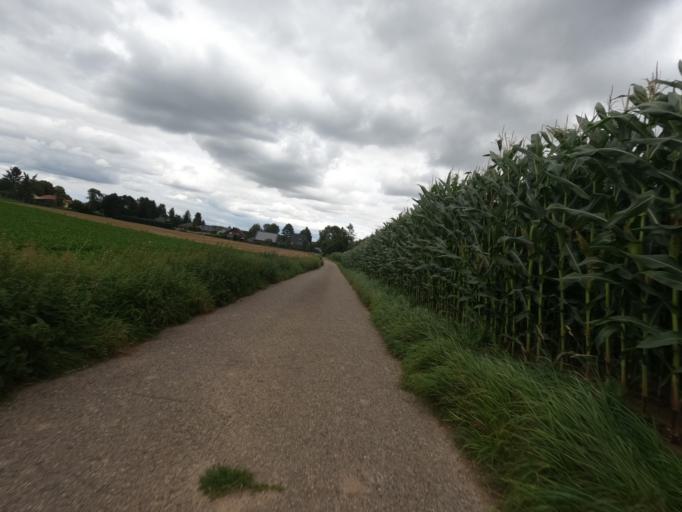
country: DE
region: North Rhine-Westphalia
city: Huckelhoven
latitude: 51.0096
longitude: 6.2252
